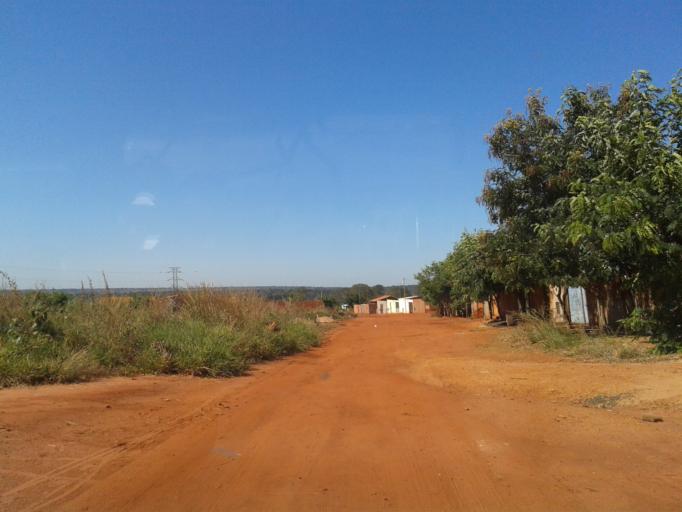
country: BR
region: Minas Gerais
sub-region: Santa Vitoria
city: Santa Vitoria
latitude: -18.8605
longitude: -50.1198
